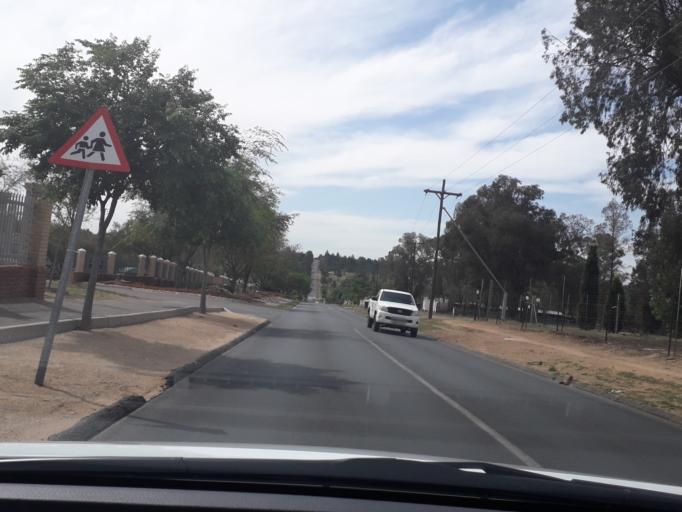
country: ZA
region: Gauteng
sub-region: City of Johannesburg Metropolitan Municipality
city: Diepsloot
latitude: -25.9812
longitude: 28.0548
